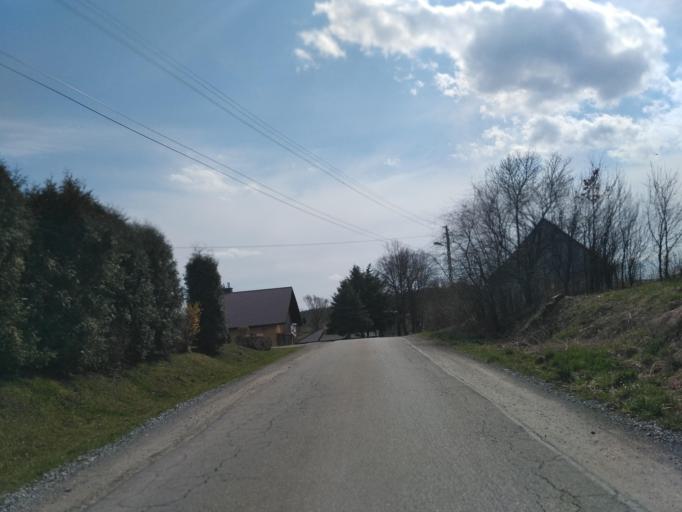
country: PL
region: Subcarpathian Voivodeship
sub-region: Powiat ropczycko-sedziszowski
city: Sedziszow Malopolski
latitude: 50.0485
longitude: 21.7172
